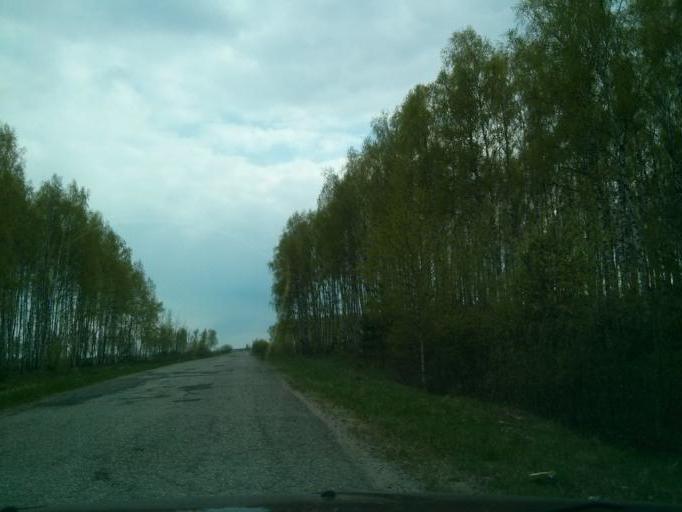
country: RU
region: Vladimir
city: Melenki
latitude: 55.3285
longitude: 41.7751
